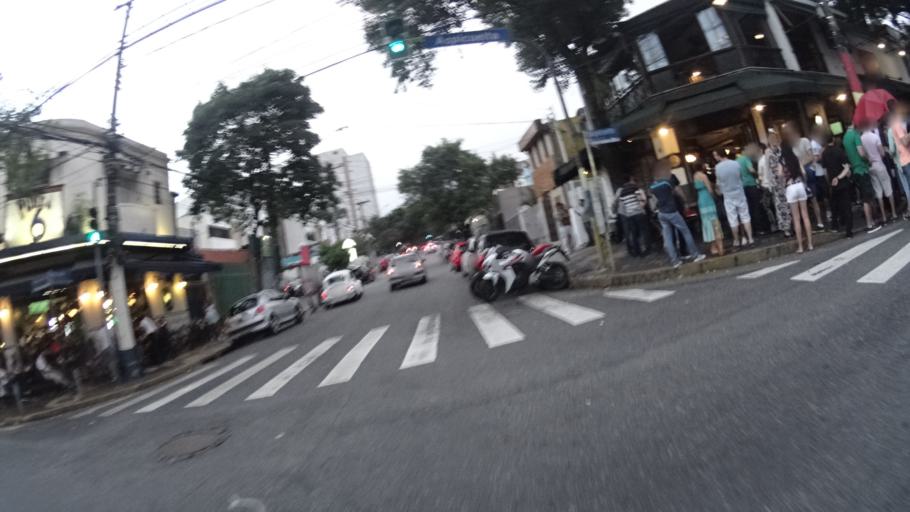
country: BR
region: Sao Paulo
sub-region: Sao Paulo
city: Sao Paulo
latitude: -23.5586
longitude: -46.6910
